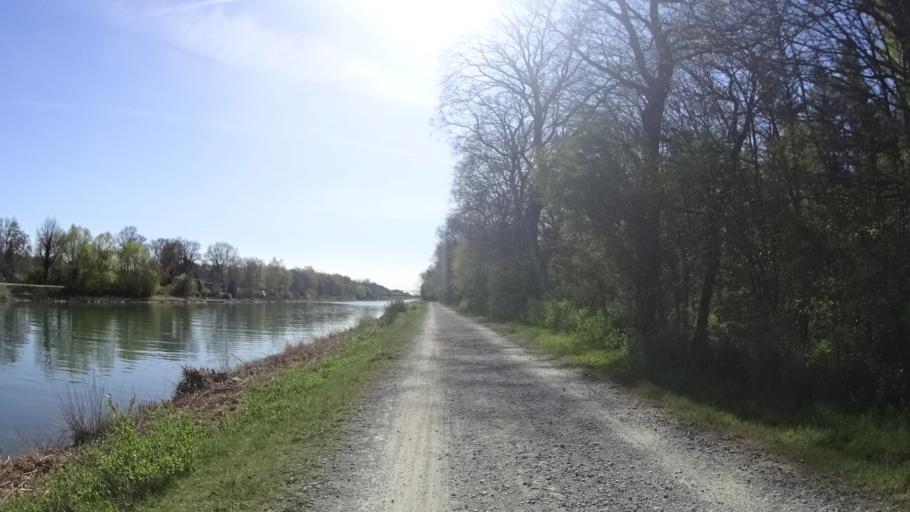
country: DE
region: North Rhine-Westphalia
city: Marl
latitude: 51.6760
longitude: 7.0441
